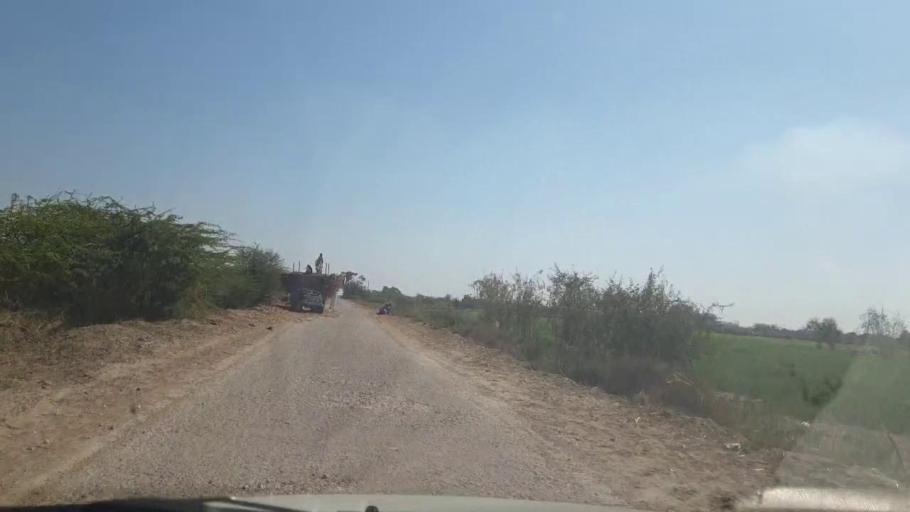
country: PK
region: Sindh
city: Mirpur Khas
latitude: 25.4854
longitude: 69.1699
